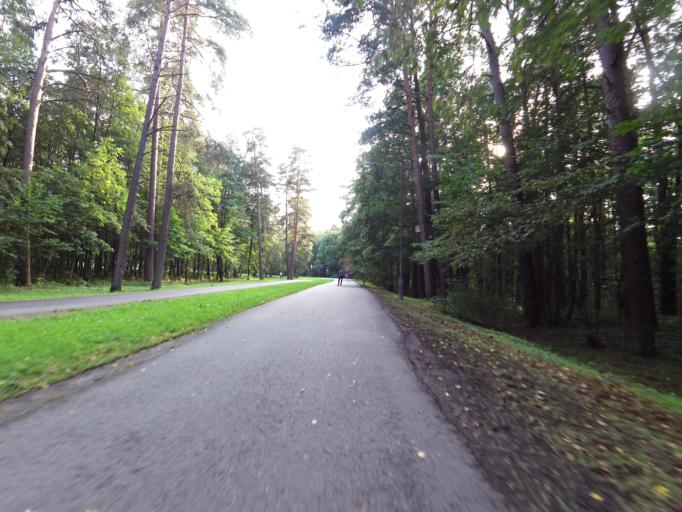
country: LT
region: Vilnius County
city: Vilkpede
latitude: 54.6860
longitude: 25.2348
